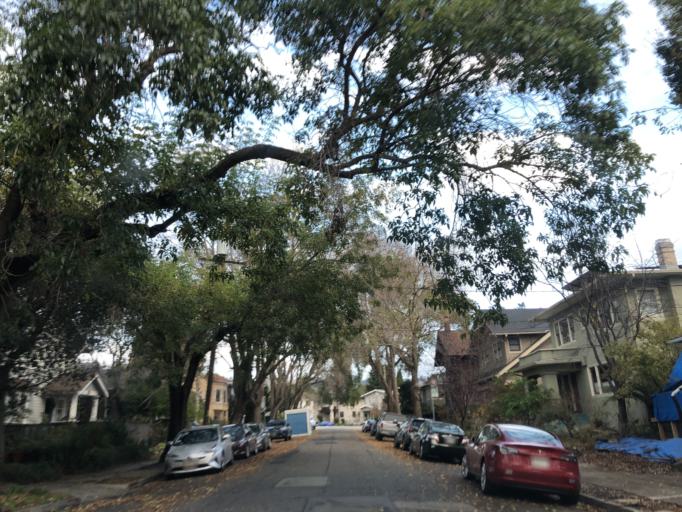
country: US
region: California
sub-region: Alameda County
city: Berkeley
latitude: 37.8470
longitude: -122.2555
